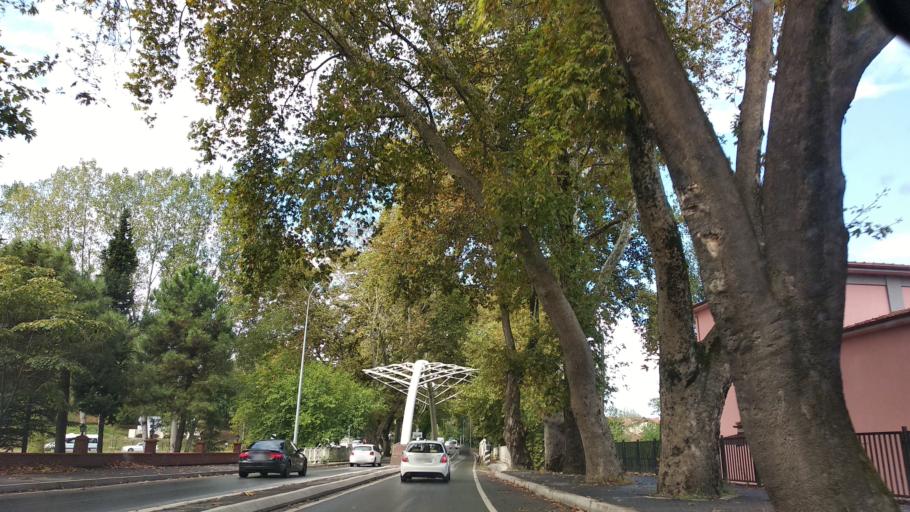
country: TR
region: Sakarya
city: Adapazari
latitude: 40.7553
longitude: 30.3763
